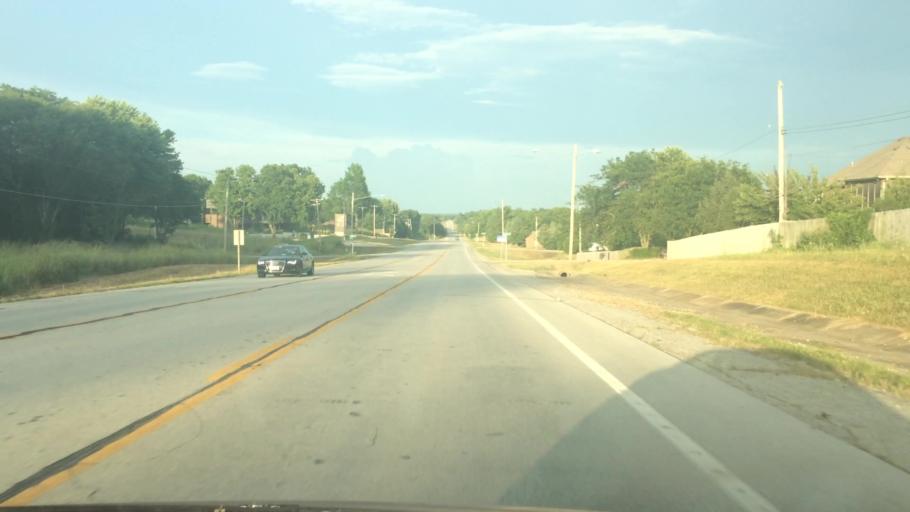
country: US
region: Missouri
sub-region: Greene County
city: Springfield
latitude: 37.1799
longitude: -93.2137
